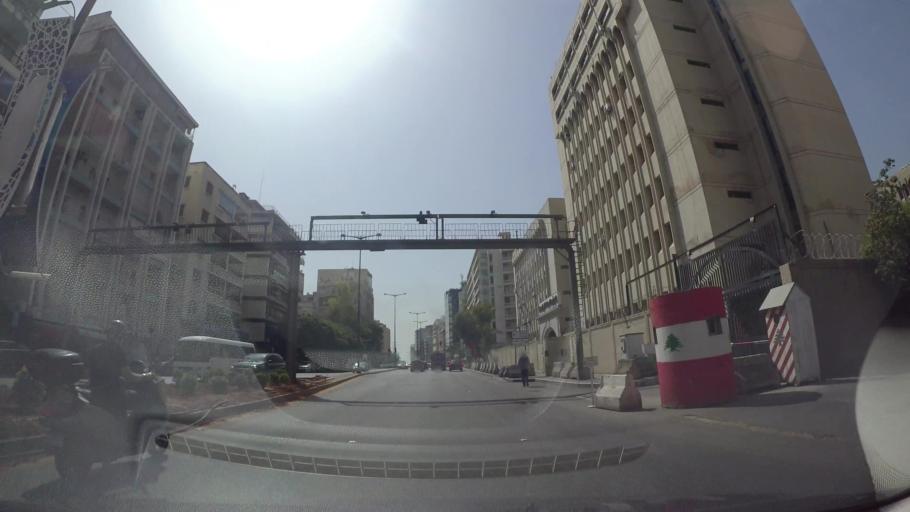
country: LB
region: Beyrouth
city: Beirut
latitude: 33.8806
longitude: 35.4914
